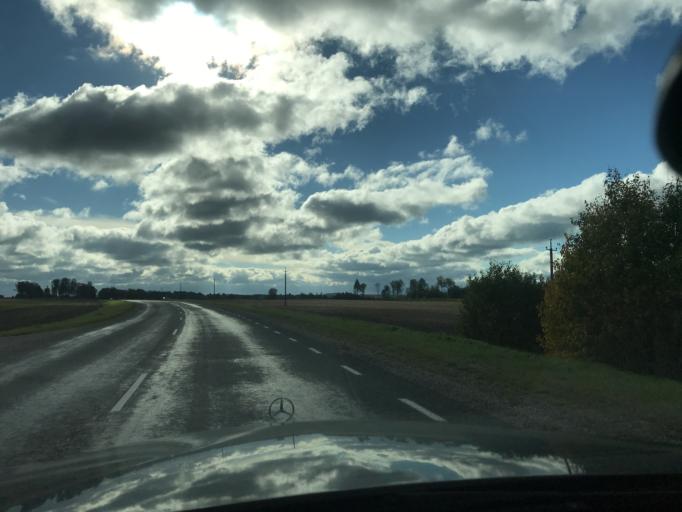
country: EE
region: Valgamaa
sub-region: Valga linn
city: Valga
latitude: 57.9714
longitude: 26.2609
